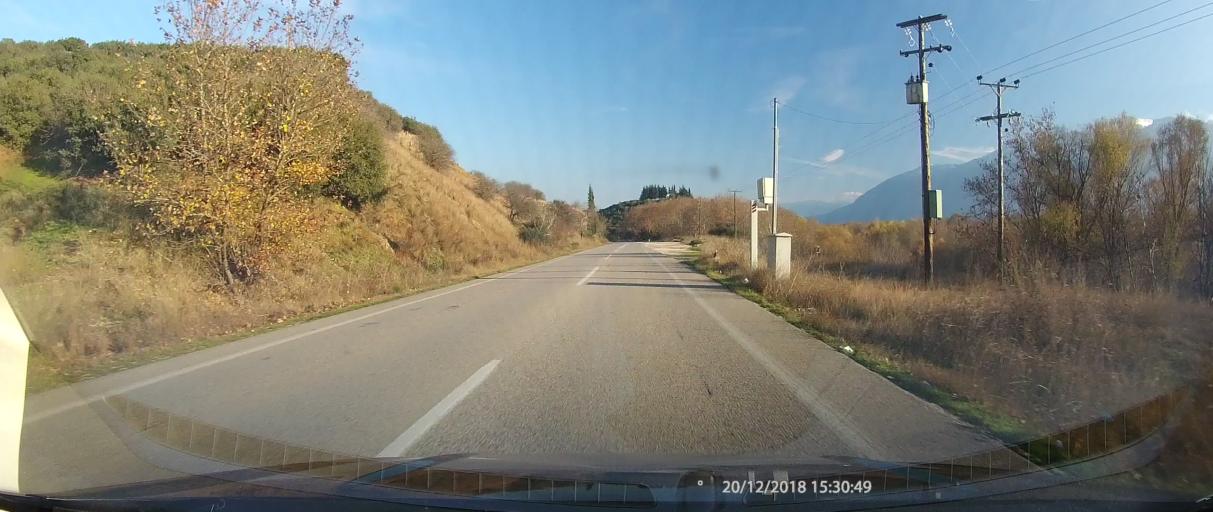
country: GR
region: Central Greece
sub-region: Nomos Fthiotidos
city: Lianokladhion
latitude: 38.9342
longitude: 22.2289
